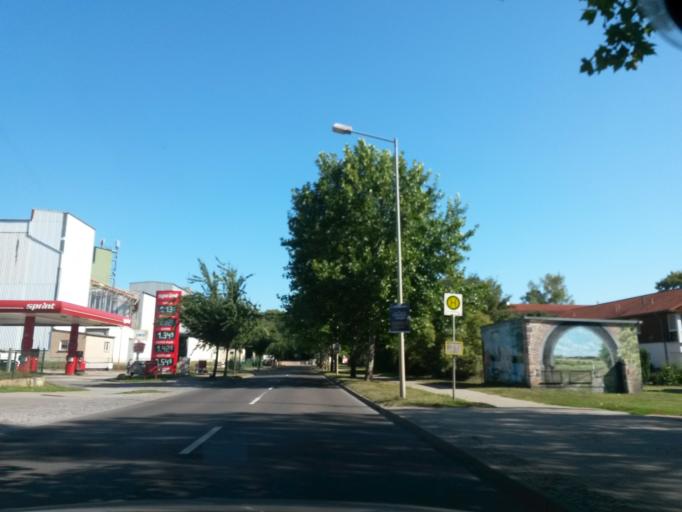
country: DE
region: Brandenburg
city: Prenzlau
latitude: 53.3039
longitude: 13.8238
